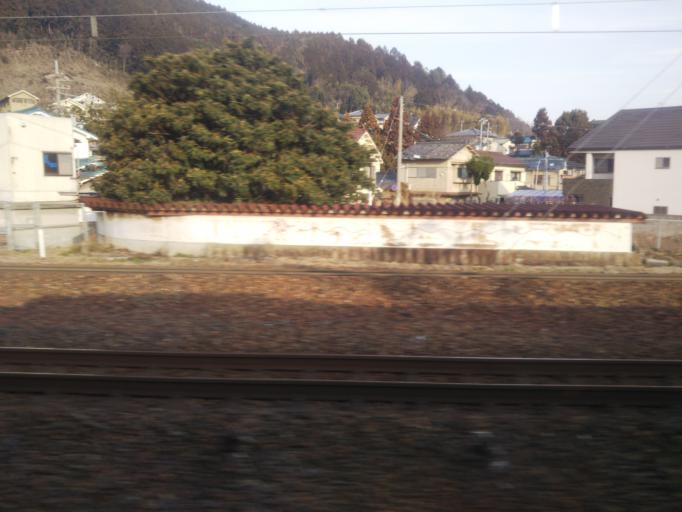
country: JP
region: Kyoto
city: Kyoto
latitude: 34.9895
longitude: 135.7997
